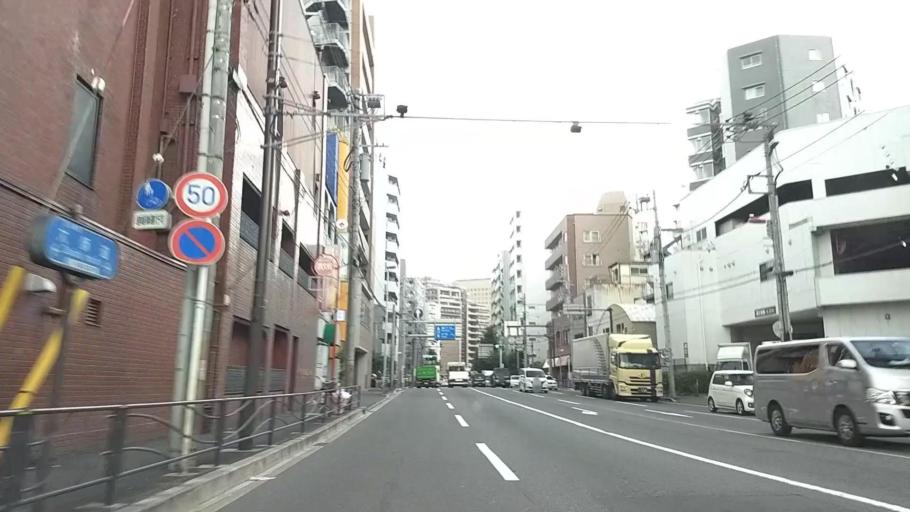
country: JP
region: Kanagawa
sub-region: Kawasaki-shi
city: Kawasaki
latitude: 35.5343
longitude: 139.7074
